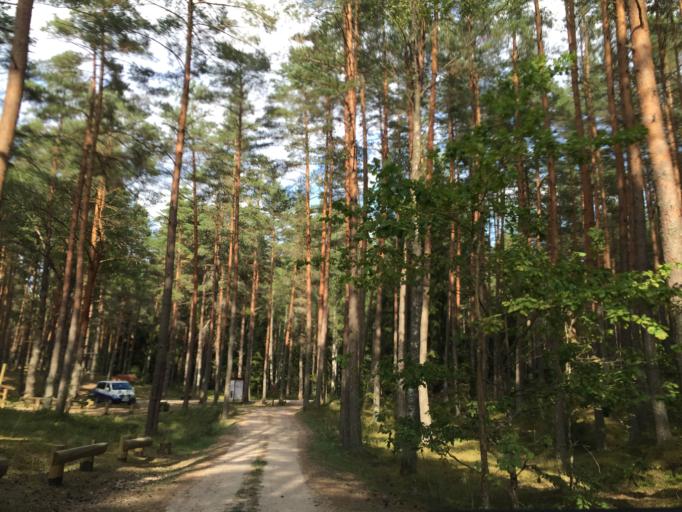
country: LV
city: Tireli
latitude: 56.8657
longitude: 23.6600
